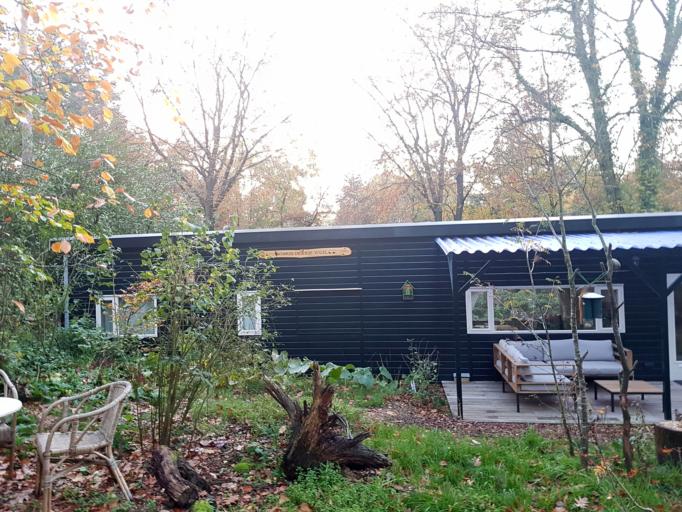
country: NL
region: Gelderland
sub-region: Gemeente Groesbeek
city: Groesbeek
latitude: 51.7836
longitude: 5.8940
